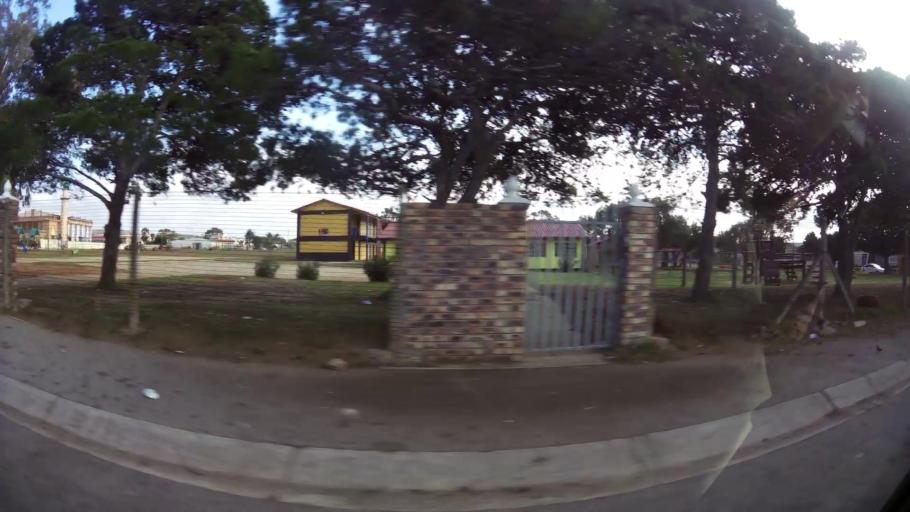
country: ZA
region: Eastern Cape
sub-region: Nelson Mandela Bay Metropolitan Municipality
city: Port Elizabeth
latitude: -33.9195
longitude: 25.5623
